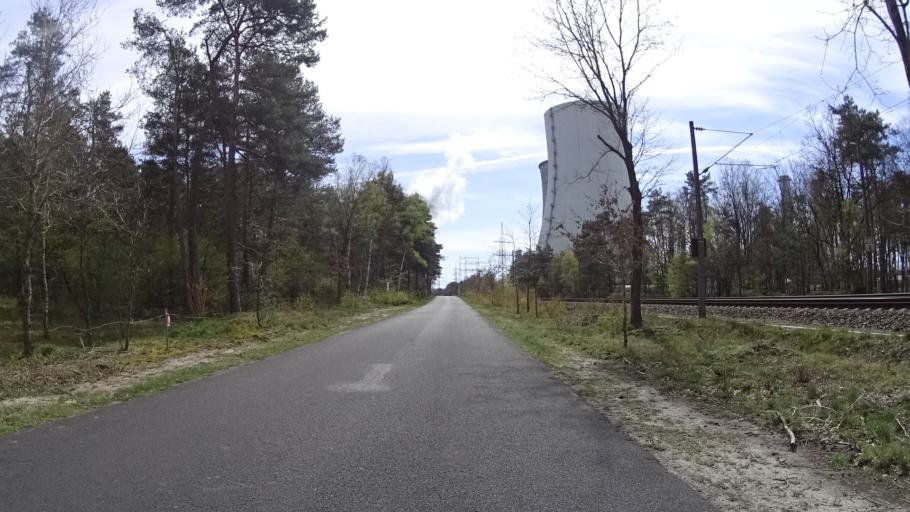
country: DE
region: Lower Saxony
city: Lingen
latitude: 52.4864
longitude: 7.3050
